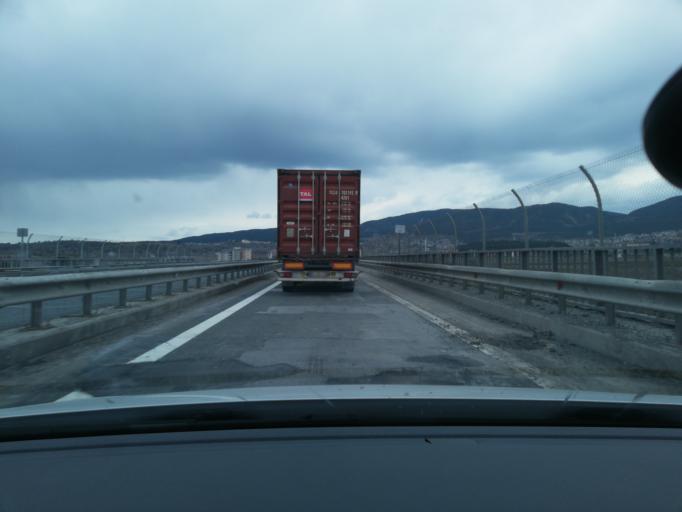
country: TR
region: Bolu
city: Gerede
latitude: 40.7786
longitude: 32.2105
